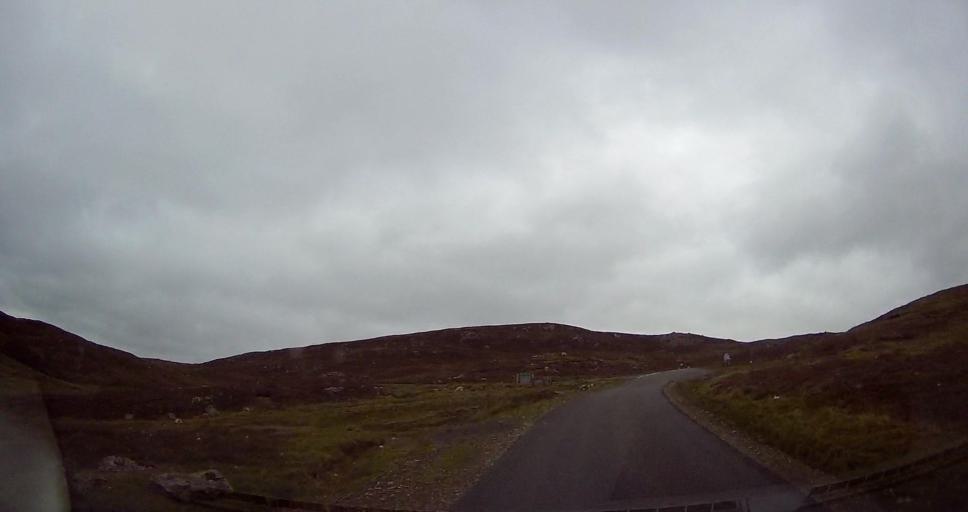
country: GB
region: Scotland
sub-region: Shetland Islands
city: Lerwick
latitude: 60.3397
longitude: -1.3175
